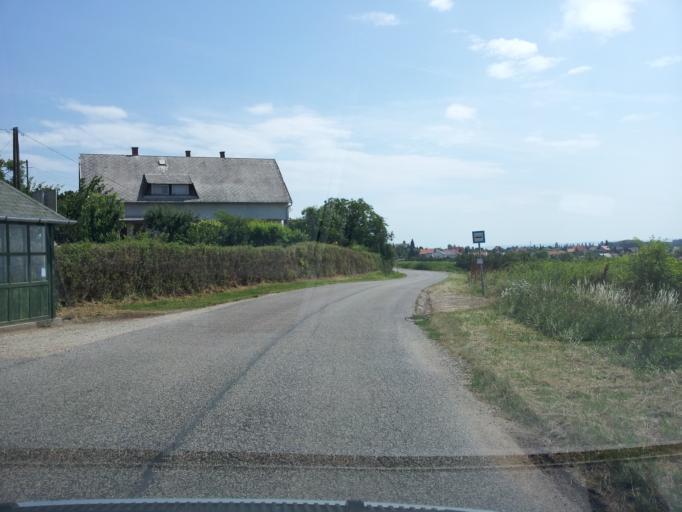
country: HU
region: Veszprem
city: Csopak
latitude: 46.9821
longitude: 17.9314
